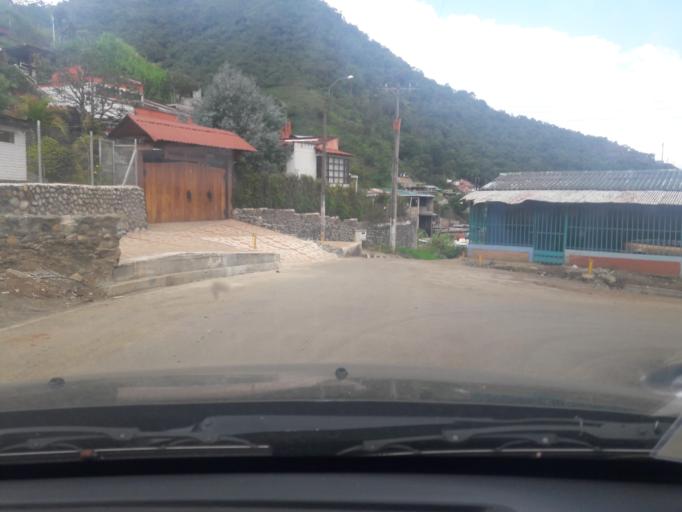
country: CO
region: Valle del Cauca
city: Cali
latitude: 3.4681
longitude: -76.6311
